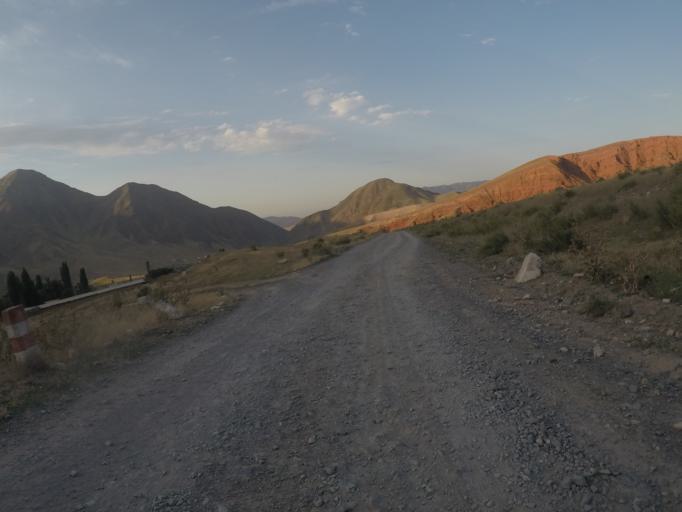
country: KG
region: Chuy
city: Bishkek
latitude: 42.6607
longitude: 74.6500
